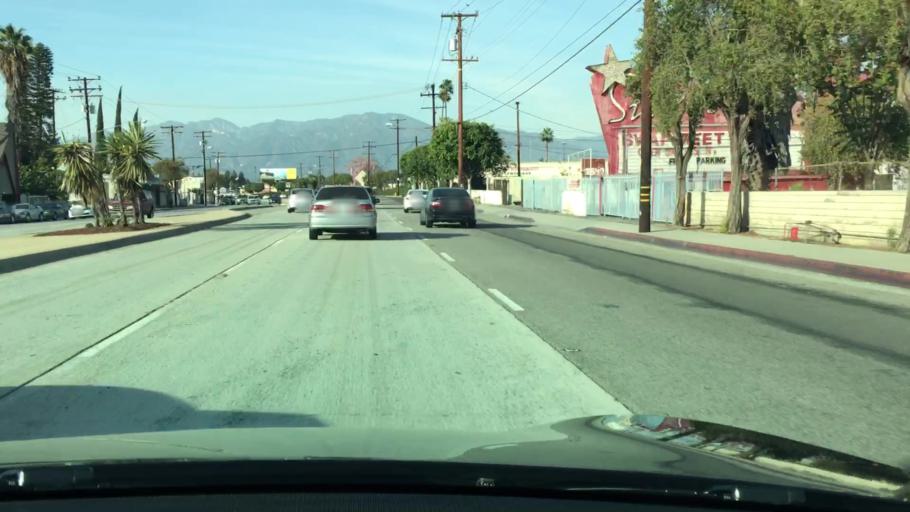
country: US
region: California
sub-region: Los Angeles County
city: South El Monte
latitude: 34.0581
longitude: -118.0643
